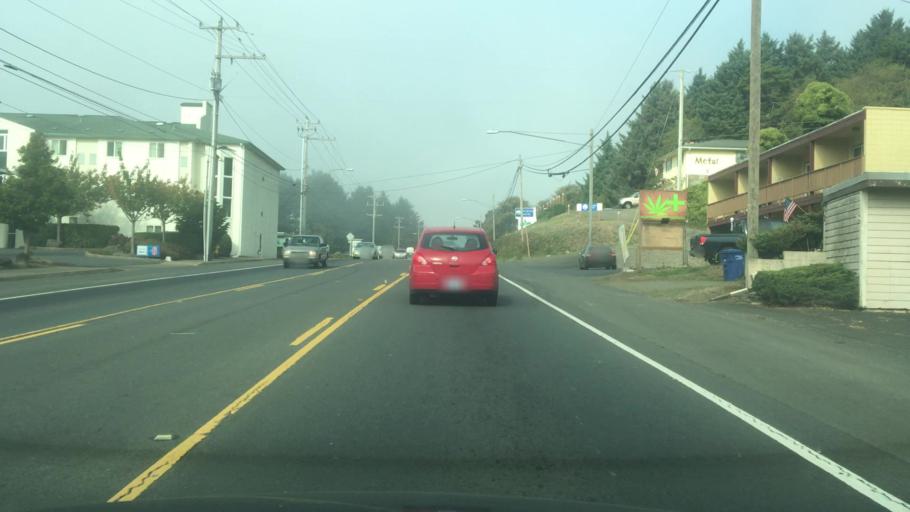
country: US
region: Oregon
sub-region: Lincoln County
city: Lincoln City
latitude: 44.9904
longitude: -124.0060
